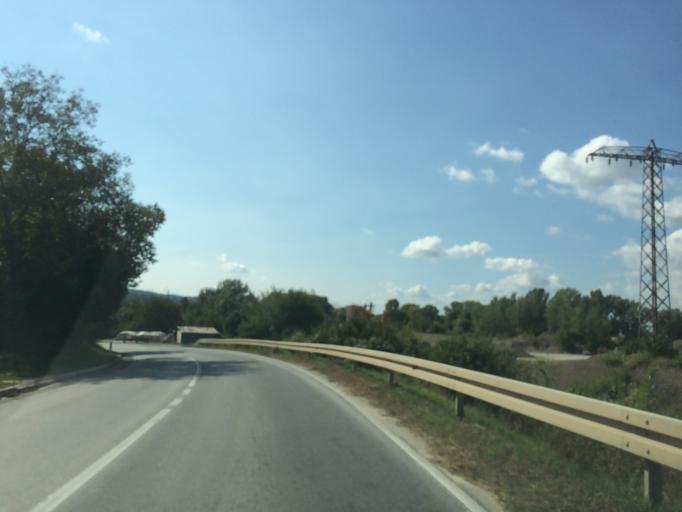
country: RS
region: Autonomna Pokrajina Vojvodina
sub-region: Juznobacki Okrug
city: Novi Sad
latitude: 45.2171
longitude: 19.8115
